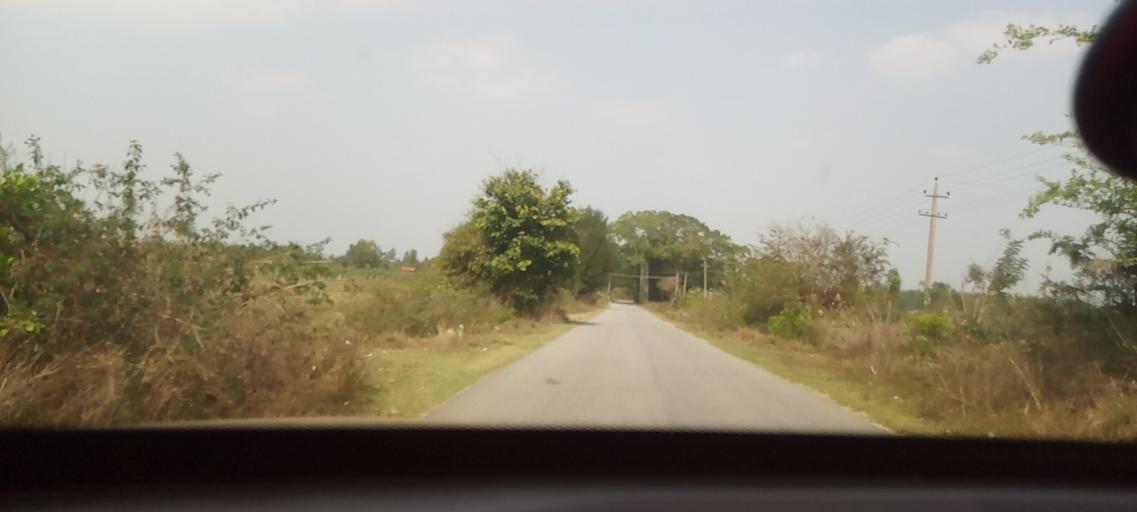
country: IN
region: Karnataka
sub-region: Hassan
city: Belur
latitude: 13.1755
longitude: 75.8188
